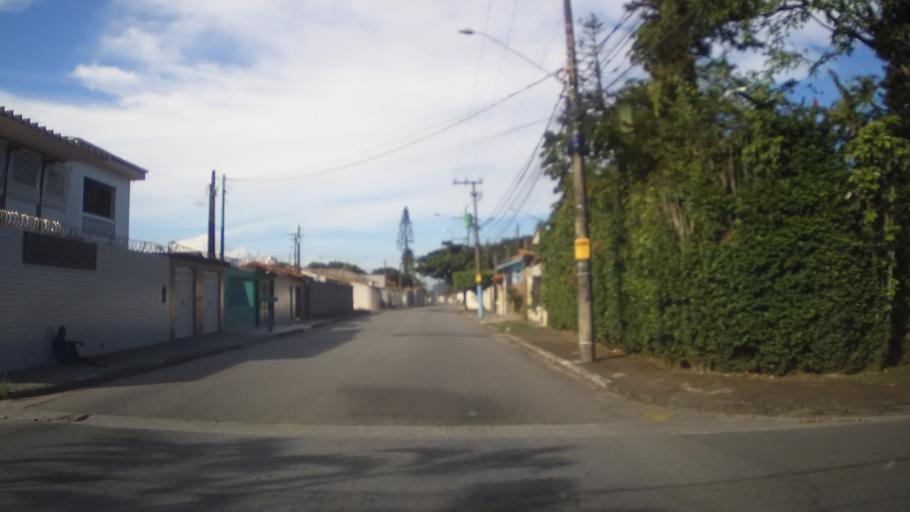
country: BR
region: Sao Paulo
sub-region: Itanhaem
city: Itanhaem
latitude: -24.1690
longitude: -46.7601
